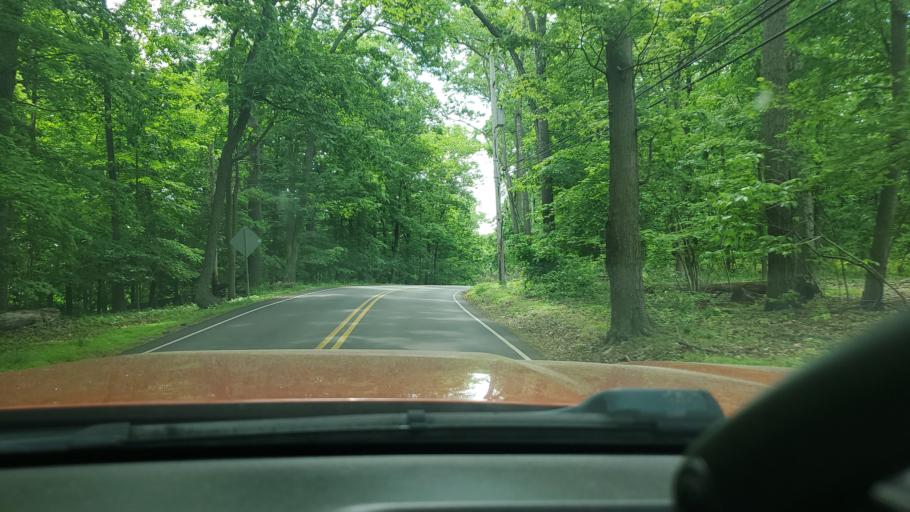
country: US
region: Pennsylvania
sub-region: Montgomery County
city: Red Hill
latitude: 40.3420
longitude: -75.4921
